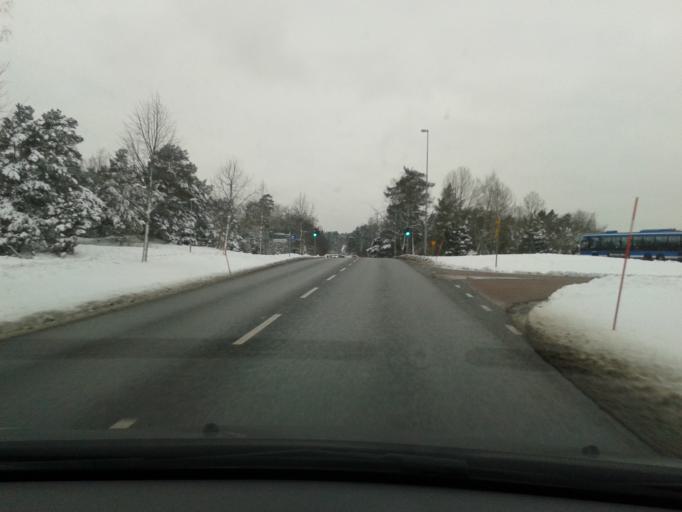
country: SE
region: Stockholm
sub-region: Nacka Kommun
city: Saltsjobaden
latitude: 59.2401
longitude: 18.2927
